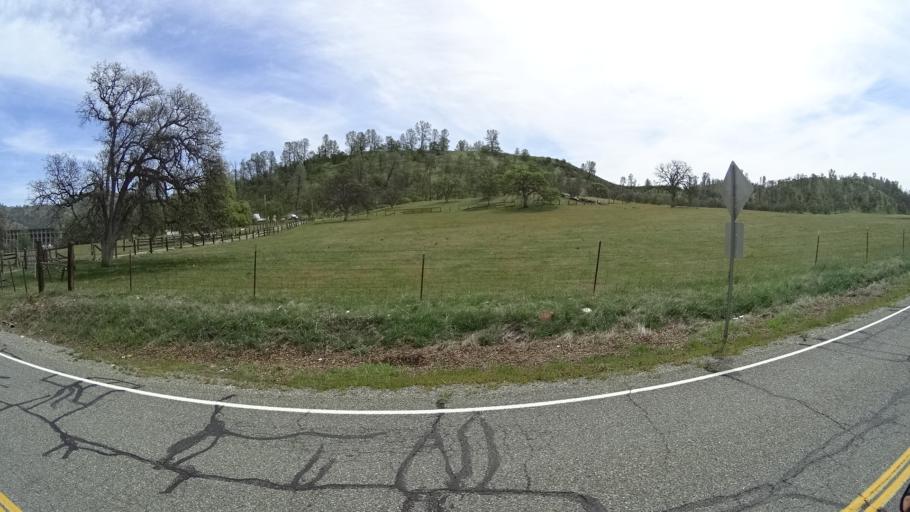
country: US
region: California
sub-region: Glenn County
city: Willows
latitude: 39.5853
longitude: -122.5377
